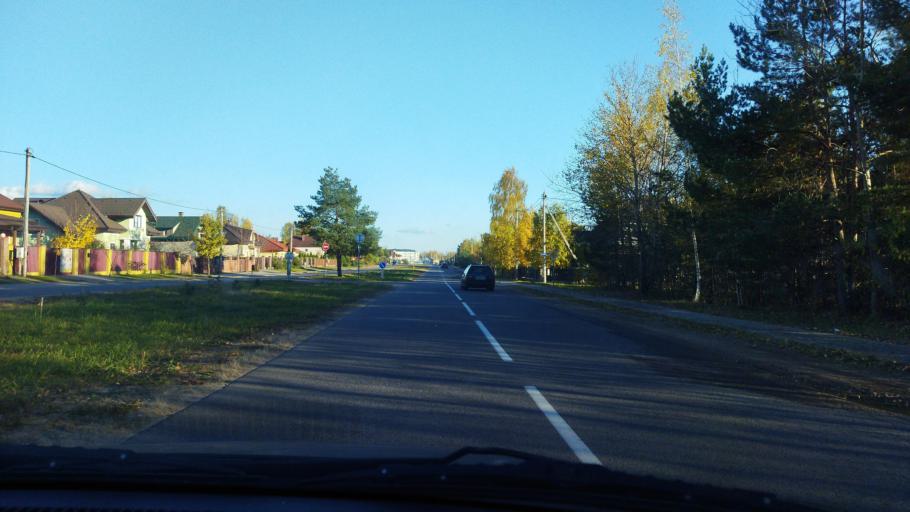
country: BY
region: Minsk
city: Kalodzishchy
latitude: 53.9158
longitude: 27.7614
